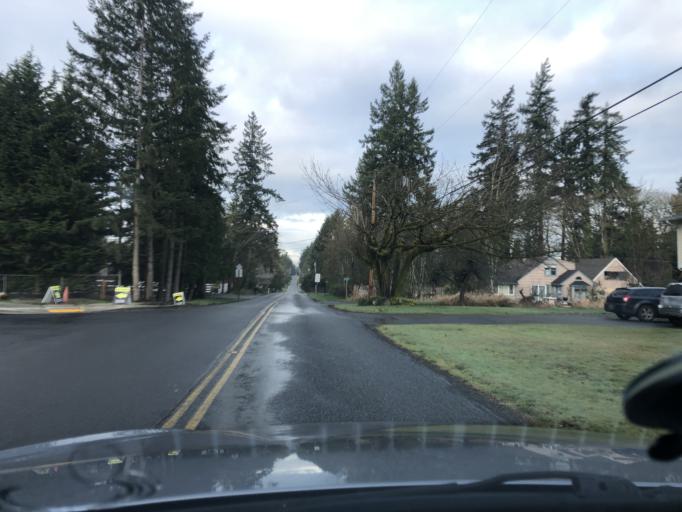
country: US
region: Washington
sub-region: Pierce County
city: Edgewood
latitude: 47.2428
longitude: -122.2988
